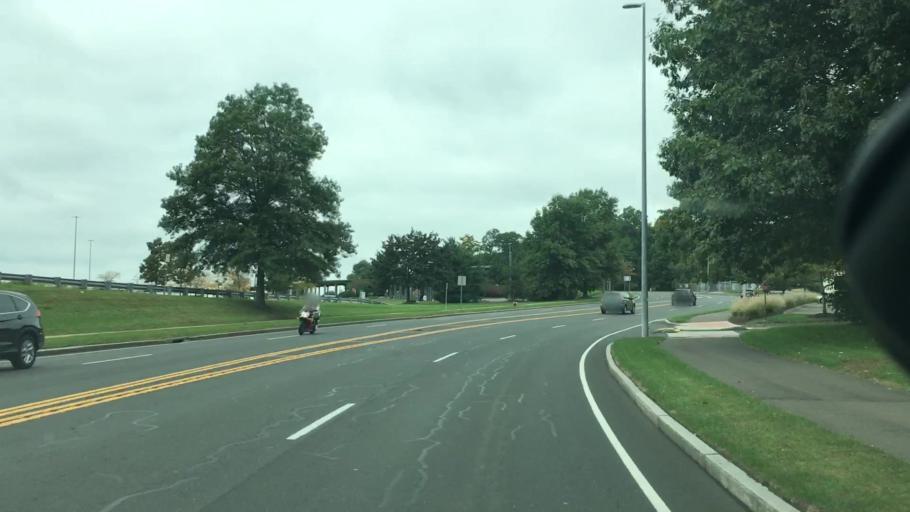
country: US
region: Connecticut
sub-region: Hartford County
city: Manchester
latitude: 41.8089
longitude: -72.5447
